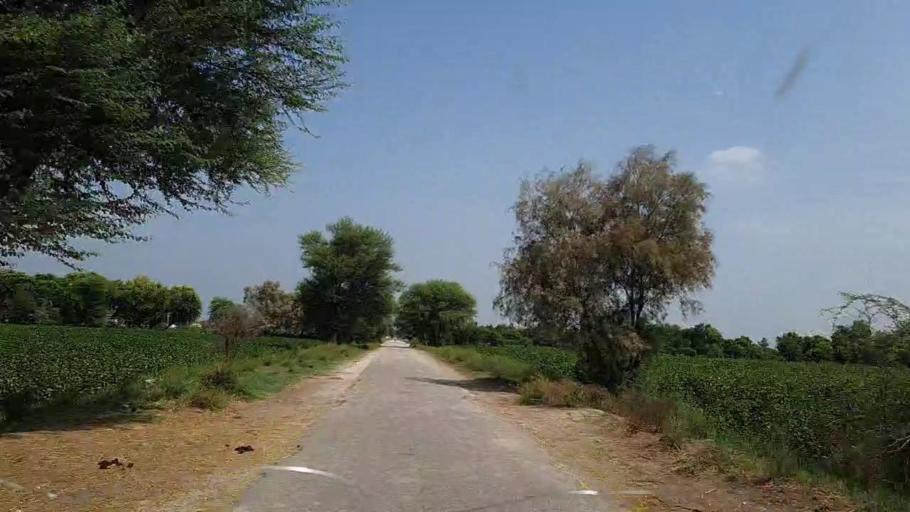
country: PK
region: Sindh
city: Adilpur
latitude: 27.8304
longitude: 69.2922
